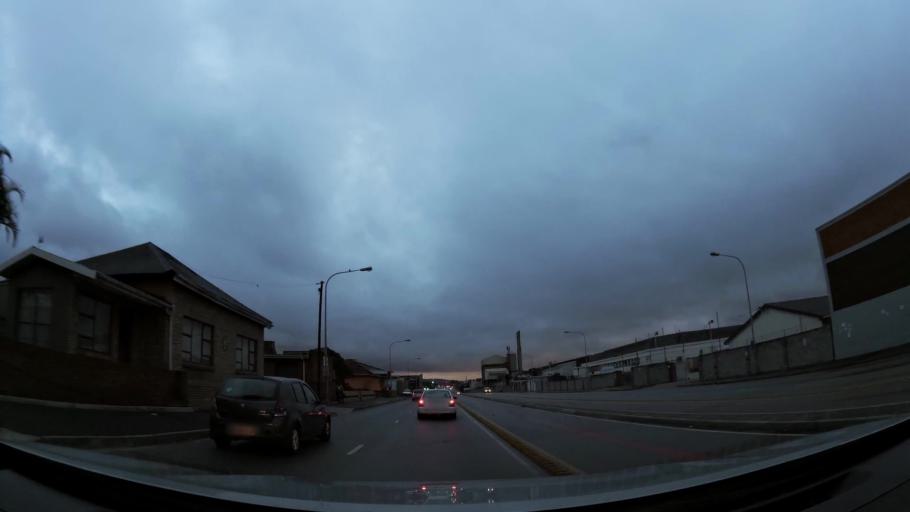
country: ZA
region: Eastern Cape
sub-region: Nelson Mandela Bay Metropolitan Municipality
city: Port Elizabeth
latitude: -33.9335
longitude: 25.5831
